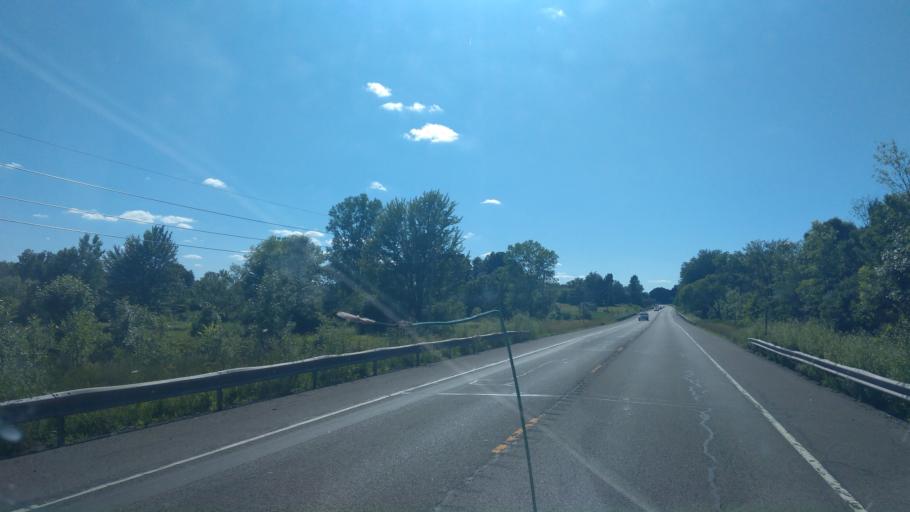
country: US
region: New York
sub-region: Seneca County
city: Seneca Falls
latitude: 42.9602
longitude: -76.8321
